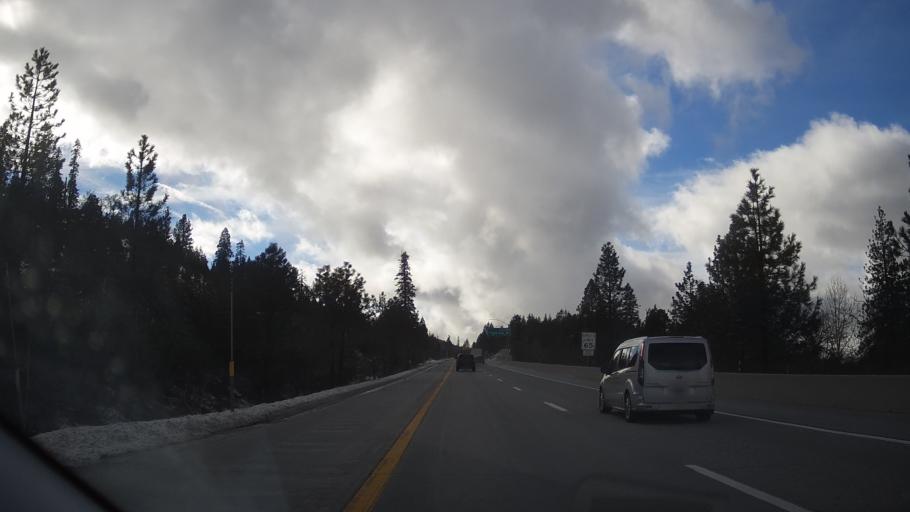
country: US
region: California
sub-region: Sierra County
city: Downieville
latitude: 39.3203
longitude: -120.6078
